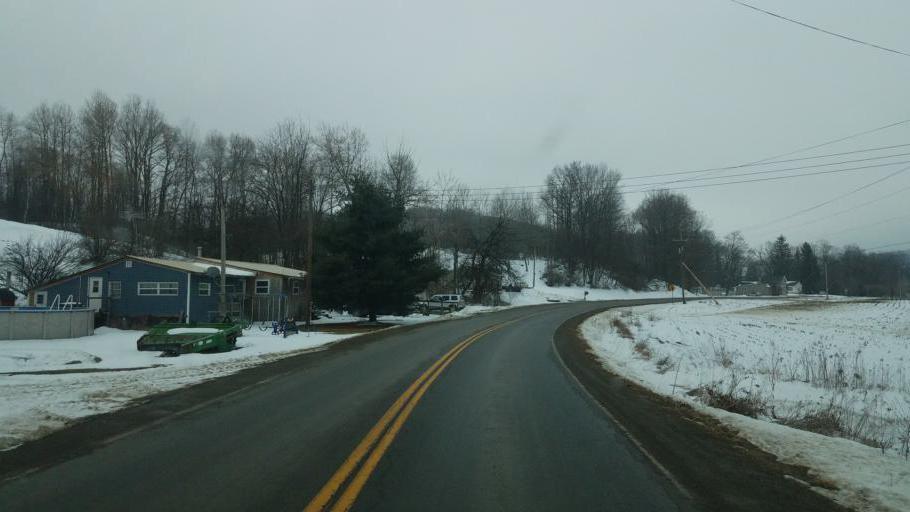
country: US
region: Pennsylvania
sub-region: Tioga County
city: Westfield
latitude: 42.0203
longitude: -77.5688
